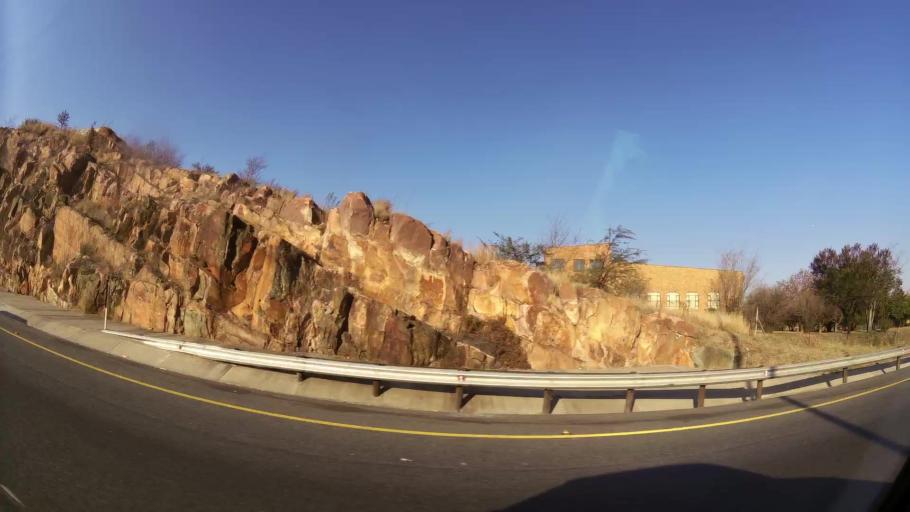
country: ZA
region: Gauteng
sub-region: Ekurhuleni Metropolitan Municipality
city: Germiston
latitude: -26.2512
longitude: 28.1227
